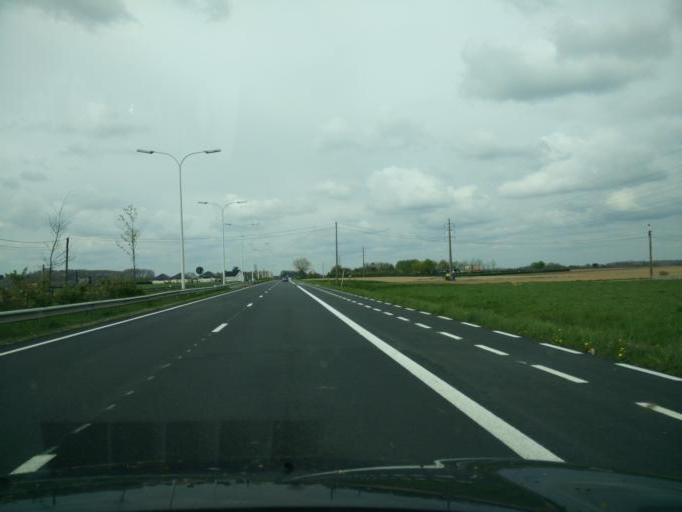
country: BE
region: Flanders
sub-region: Provincie Oost-Vlaanderen
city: Oudenaarde
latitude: 50.8843
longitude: 3.6161
